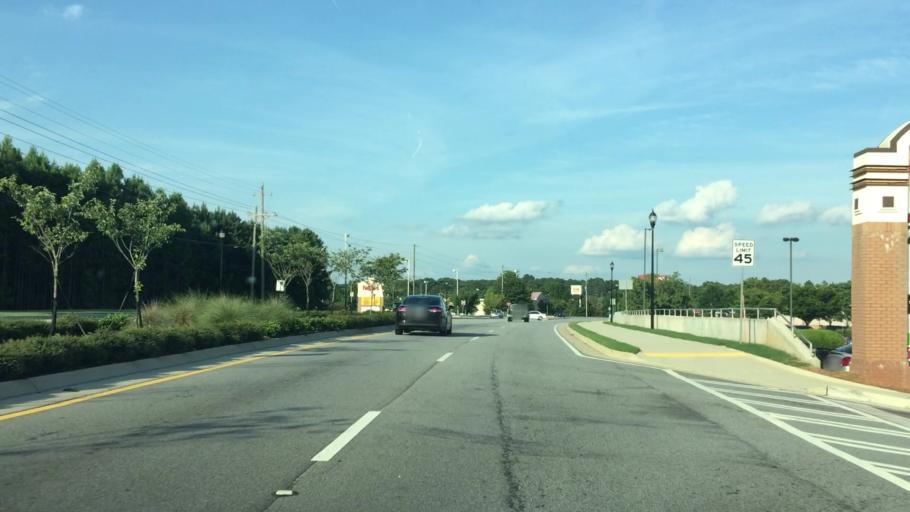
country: US
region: Georgia
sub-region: Henry County
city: Stockbridge
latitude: 33.6203
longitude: -84.2396
